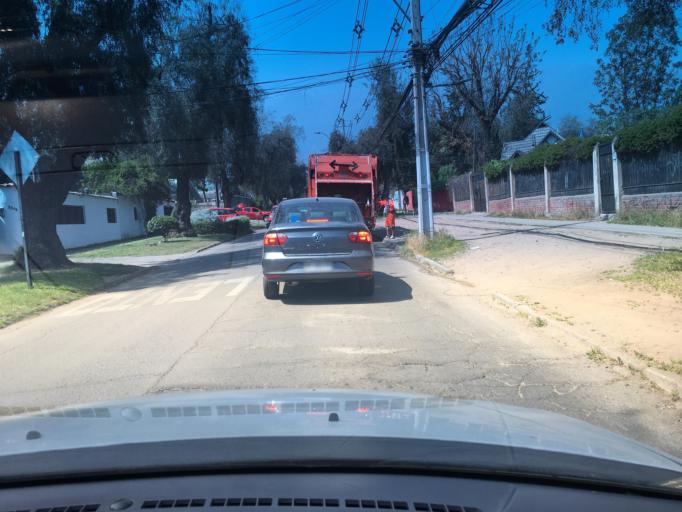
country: CL
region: Santiago Metropolitan
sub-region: Provincia de Santiago
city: Villa Presidente Frei, Nunoa, Santiago, Chile
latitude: -33.5182
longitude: -70.5608
